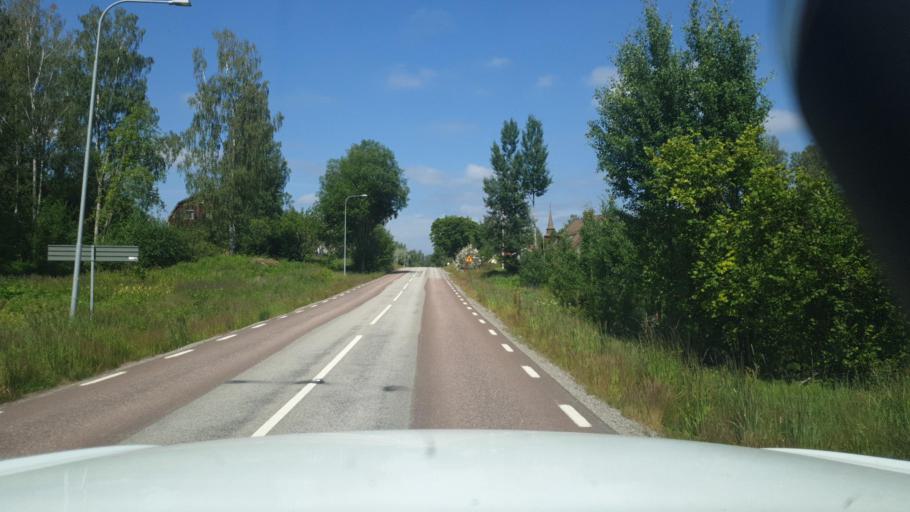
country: SE
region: Vaermland
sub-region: Arvika Kommun
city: Arvika
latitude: 59.6412
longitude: 12.4783
